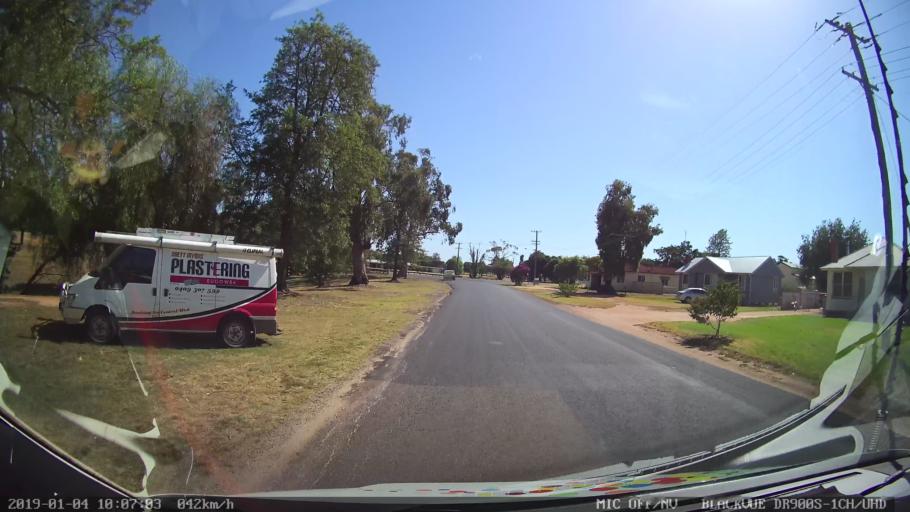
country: AU
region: New South Wales
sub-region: Cabonne
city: Canowindra
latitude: -33.4305
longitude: 148.3709
